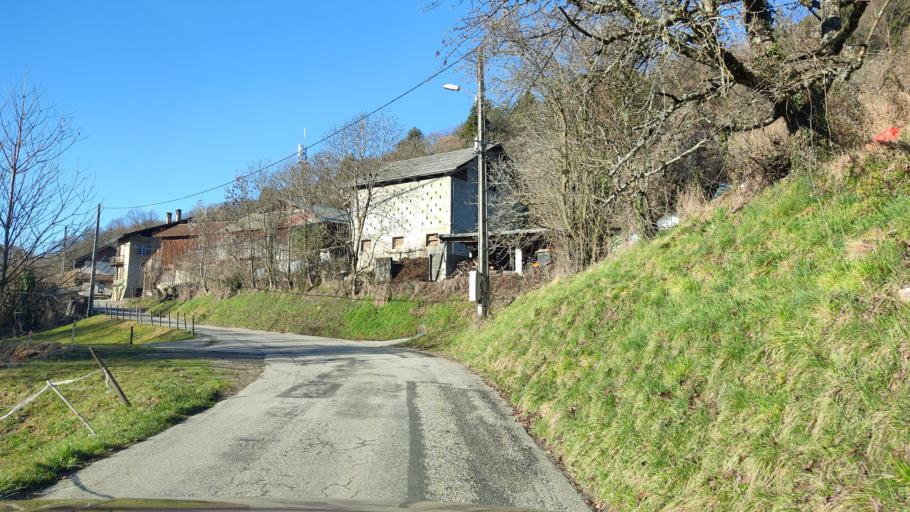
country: FR
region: Rhone-Alpes
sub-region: Departement de la Savoie
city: La Rochette
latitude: 45.4616
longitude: 6.1051
